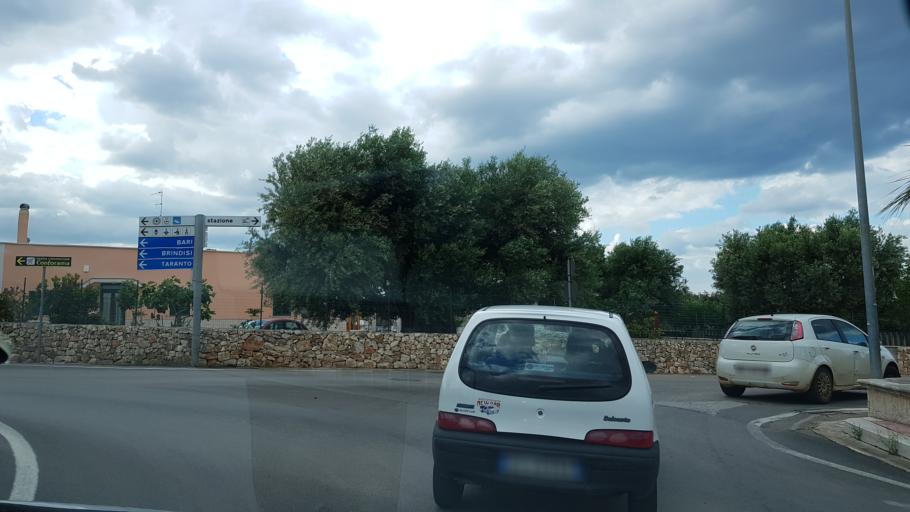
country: IT
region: Apulia
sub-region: Provincia di Brindisi
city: Fasano
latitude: 40.8491
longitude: 17.3866
